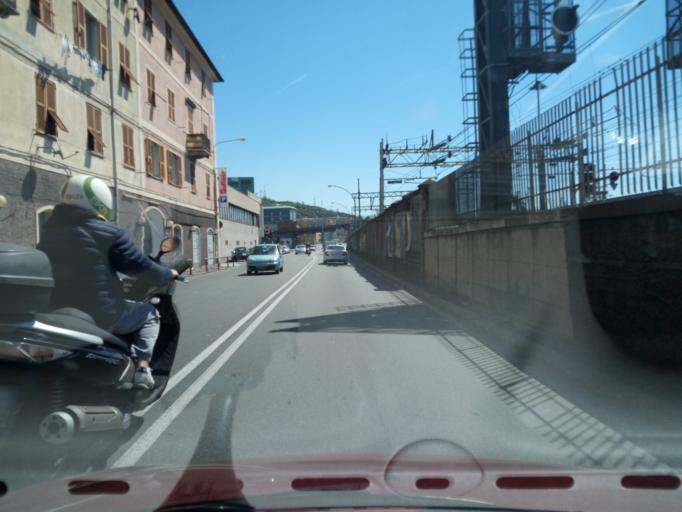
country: IT
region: Liguria
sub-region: Provincia di Genova
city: San Teodoro
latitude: 44.4221
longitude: 8.8501
